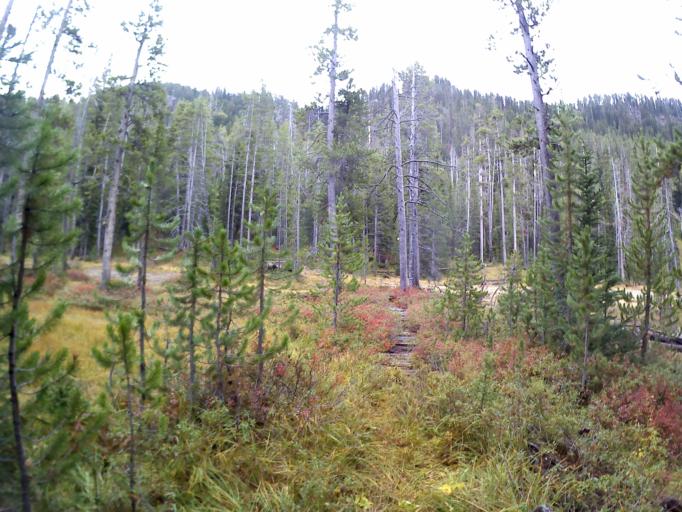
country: US
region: Montana
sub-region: Gallatin County
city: West Yellowstone
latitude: 44.4296
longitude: -110.7479
